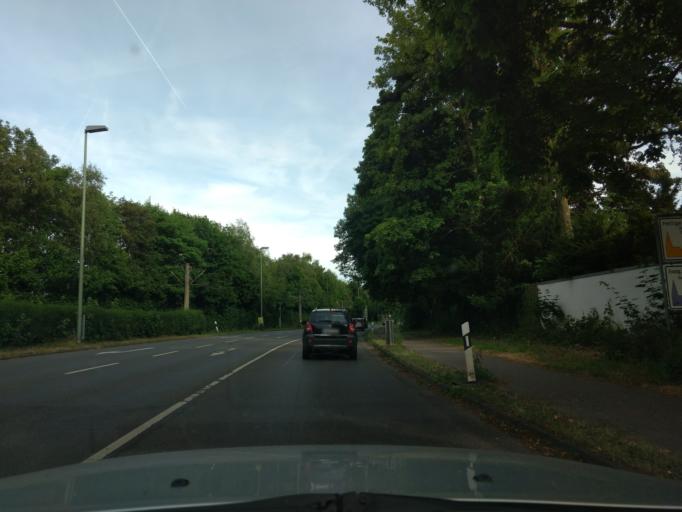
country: DE
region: North Rhine-Westphalia
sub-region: Regierungsbezirk Dusseldorf
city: Meerbusch
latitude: 51.2649
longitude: 6.6731
